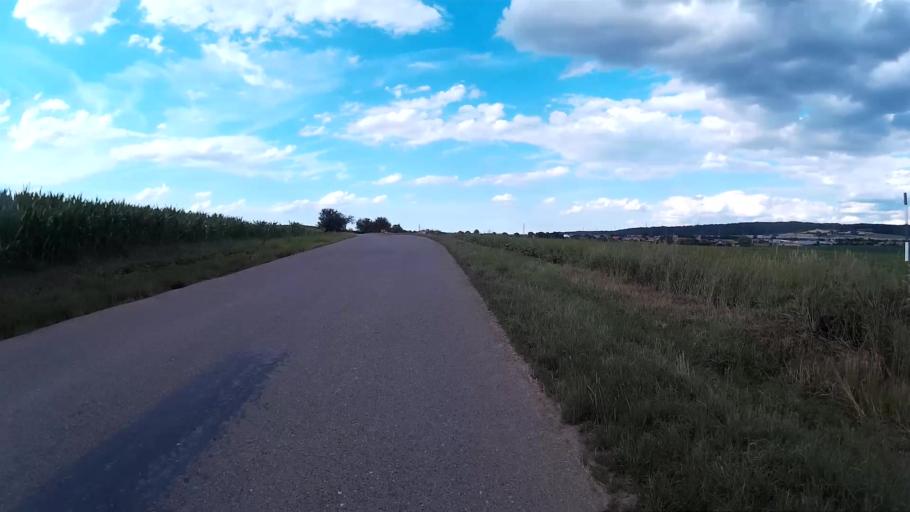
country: CZ
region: South Moravian
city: Ricany
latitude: 49.2016
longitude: 16.4030
